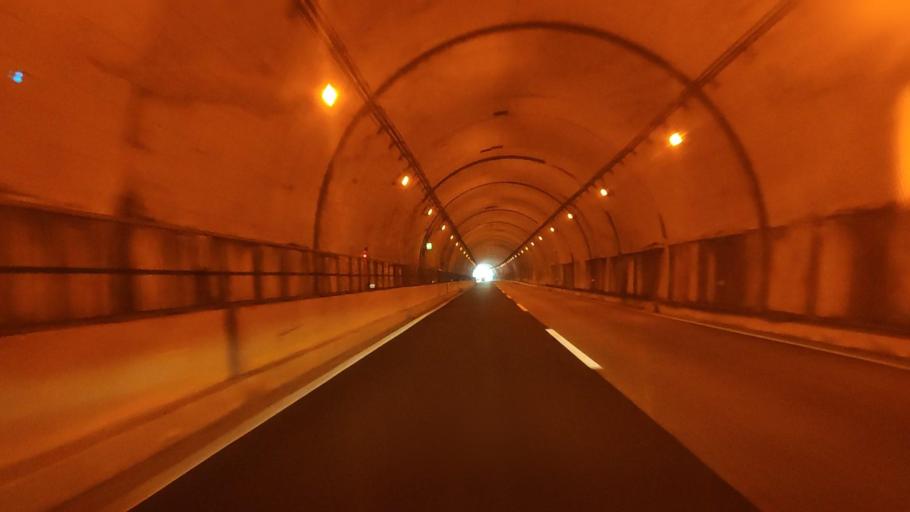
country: JP
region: Miyazaki
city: Miyazaki-shi
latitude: 31.8202
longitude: 131.2593
